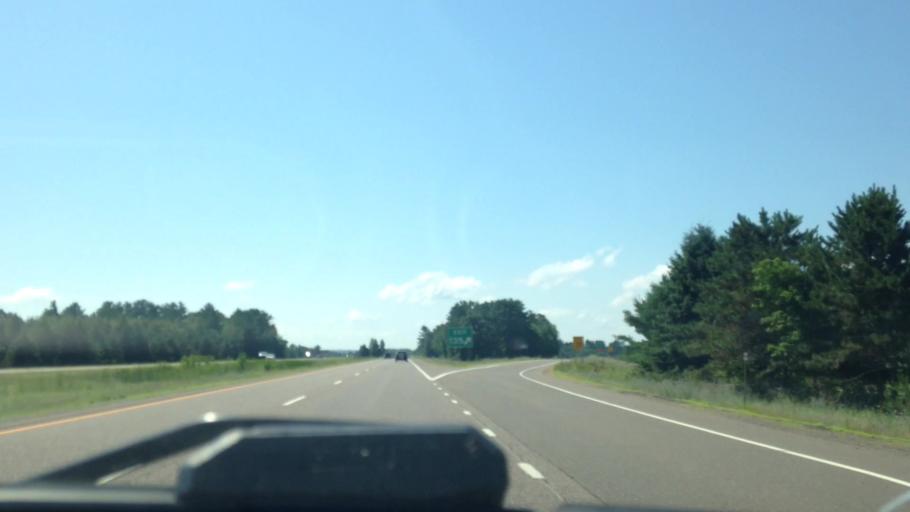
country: US
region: Wisconsin
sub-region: Barron County
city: Cameron
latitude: 45.4007
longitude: -91.7602
